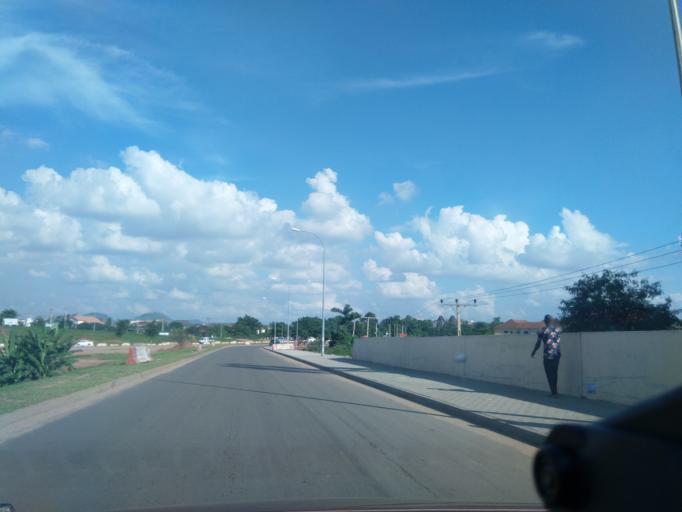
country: NG
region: Abuja Federal Capital Territory
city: Abuja
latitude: 9.0657
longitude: 7.4090
